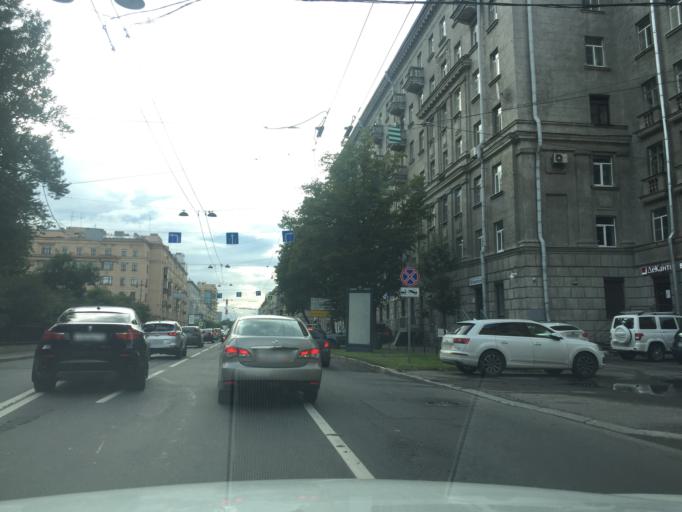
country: RU
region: St.-Petersburg
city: Kupchino
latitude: 59.8718
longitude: 30.3224
